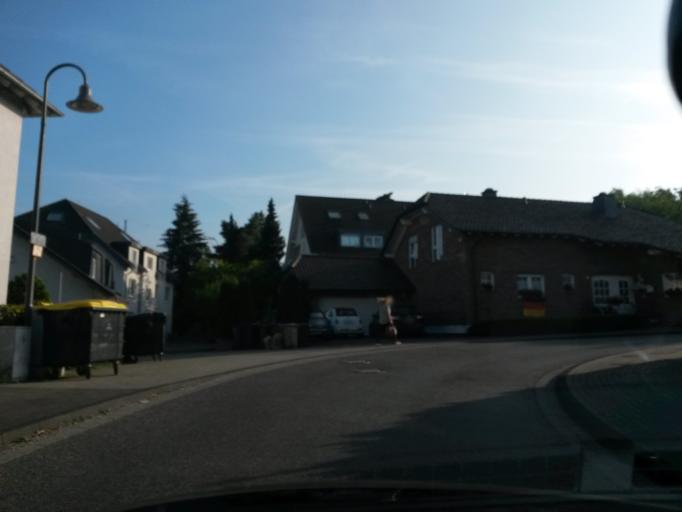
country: DE
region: North Rhine-Westphalia
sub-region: Regierungsbezirk Koln
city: Alfter
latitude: 50.7145
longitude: 7.0219
